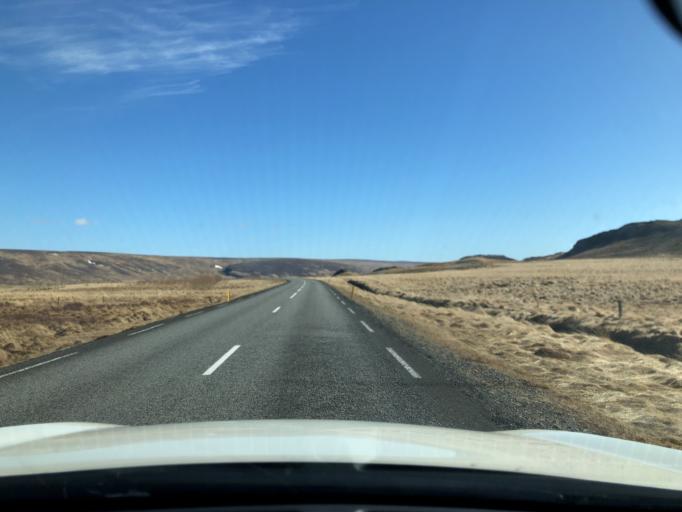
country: IS
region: South
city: Hveragerdi
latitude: 64.6797
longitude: -21.2469
